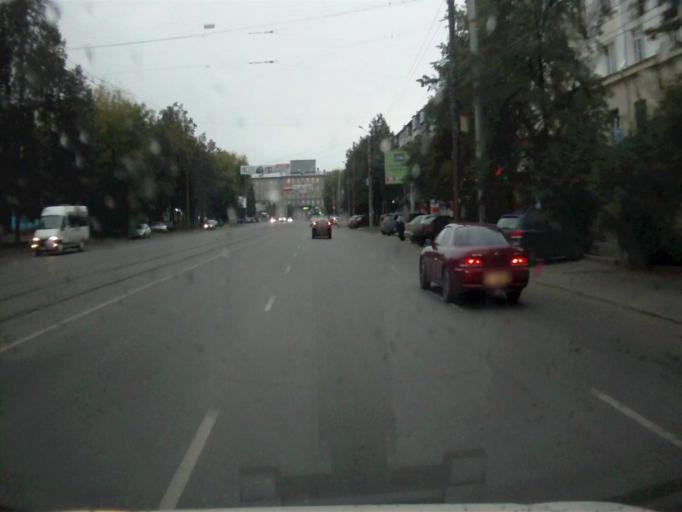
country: RU
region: Chelyabinsk
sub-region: Gorod Chelyabinsk
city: Chelyabinsk
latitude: 55.1805
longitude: 61.3994
